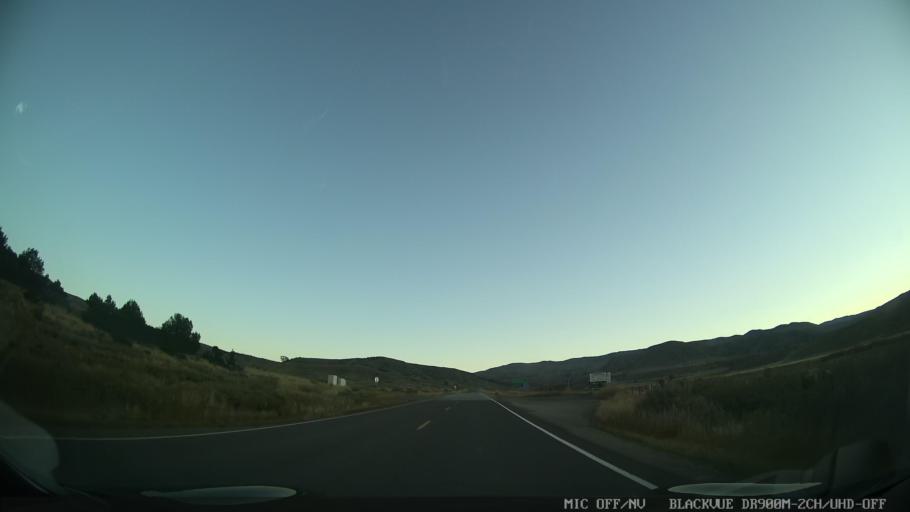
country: US
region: Colorado
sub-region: Eagle County
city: Edwards
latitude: 39.7357
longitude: -106.6794
